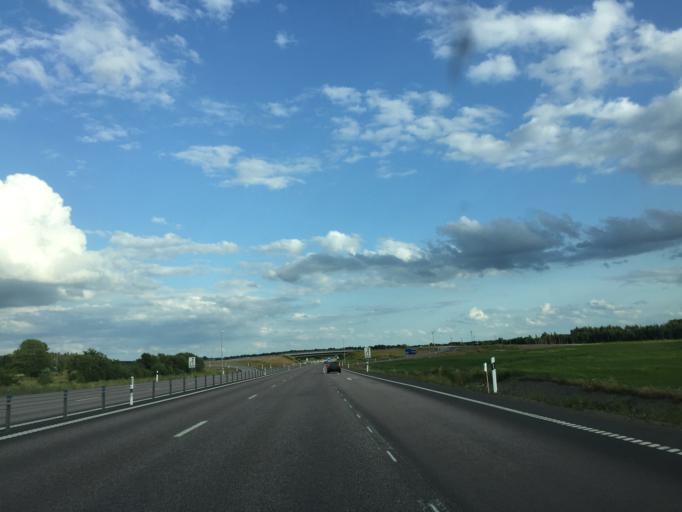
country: SE
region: OEstergoetland
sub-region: Motala Kommun
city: Motala
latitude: 58.5110
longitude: 15.0219
